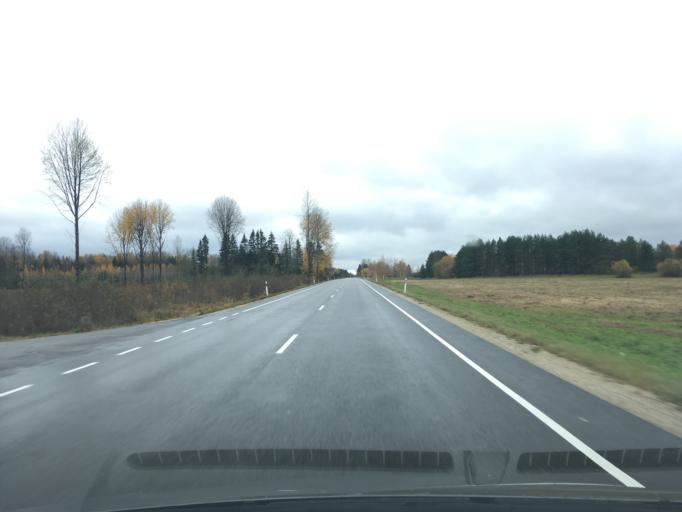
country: EE
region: Jogevamaa
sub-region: Tabivere vald
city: Tabivere
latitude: 58.4478
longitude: 26.5160
